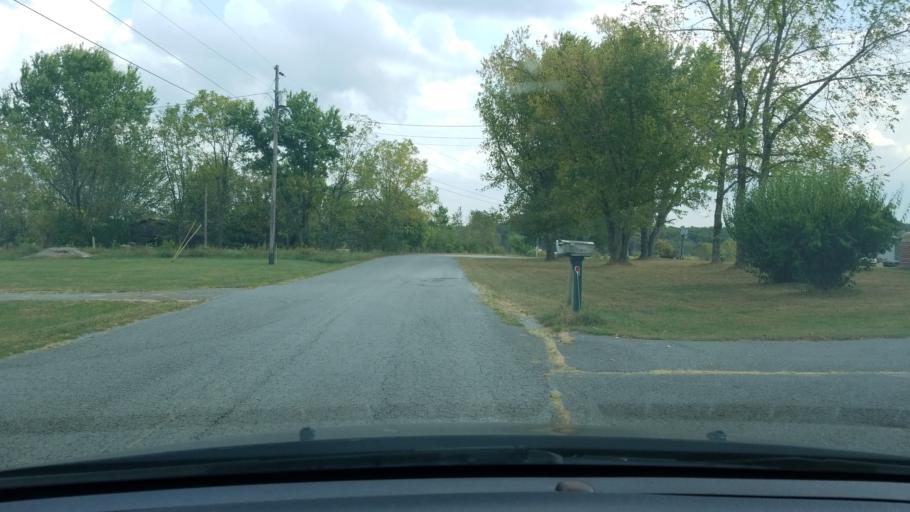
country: US
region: Tennessee
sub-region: Cumberland County
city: Crossville
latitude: 35.9394
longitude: -85.0995
